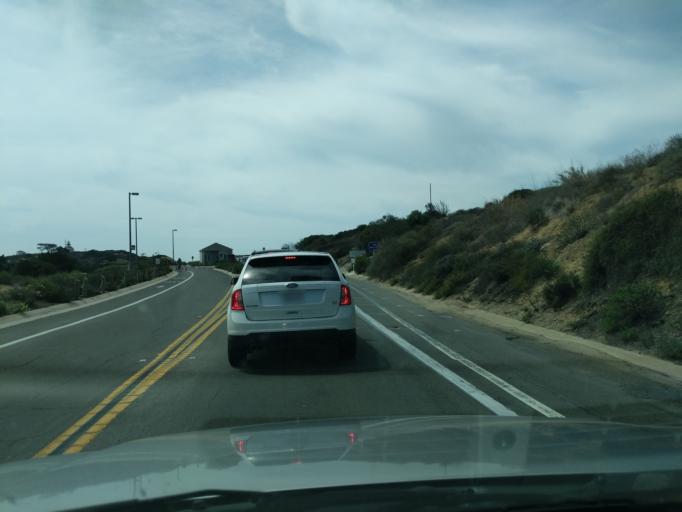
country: US
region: California
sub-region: San Diego County
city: Coronado
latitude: 32.6780
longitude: -117.2434
